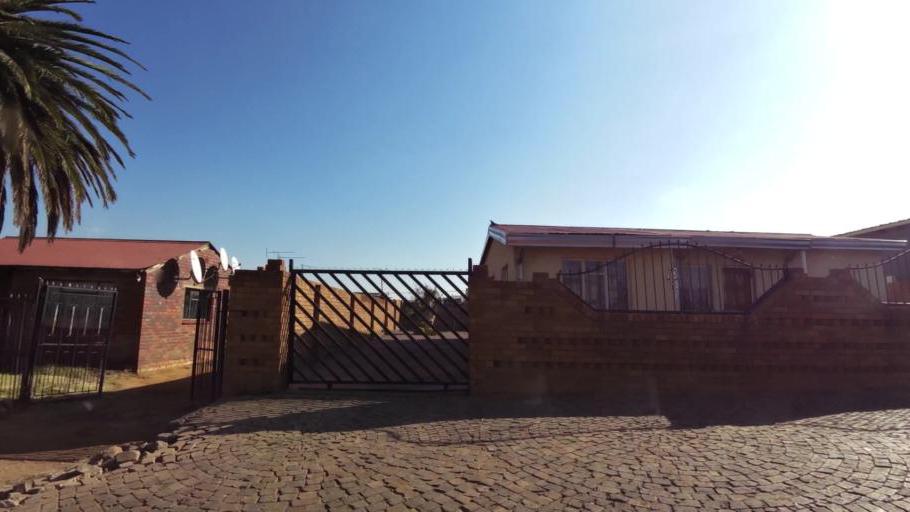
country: ZA
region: Gauteng
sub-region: City of Johannesburg Metropolitan Municipality
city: Soweto
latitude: -26.2467
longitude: 27.9237
